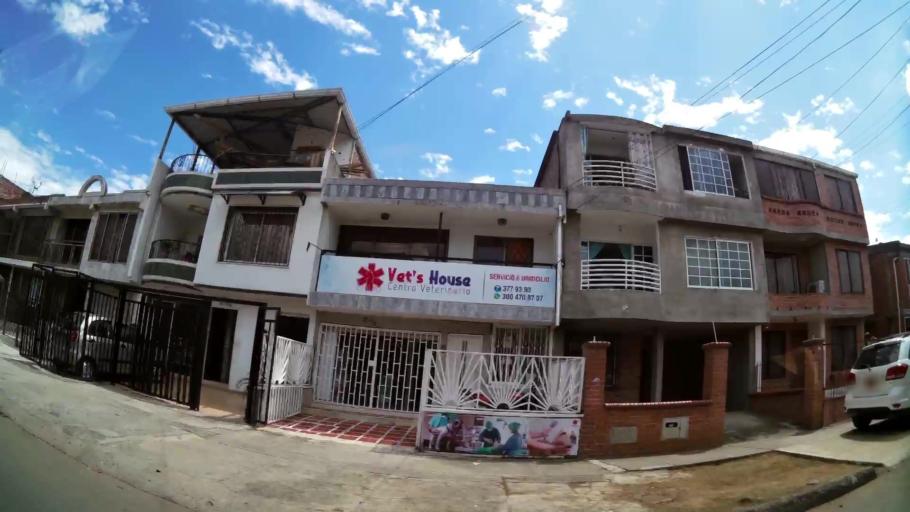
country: CO
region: Valle del Cauca
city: Cali
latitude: 3.3819
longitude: -76.5209
